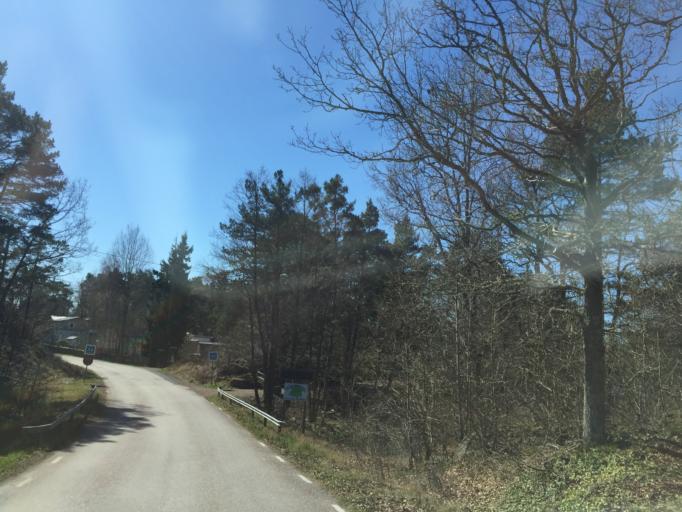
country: SE
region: Kalmar
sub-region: Oskarshamns Kommun
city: Oskarshamn
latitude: 57.2340
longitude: 16.4799
